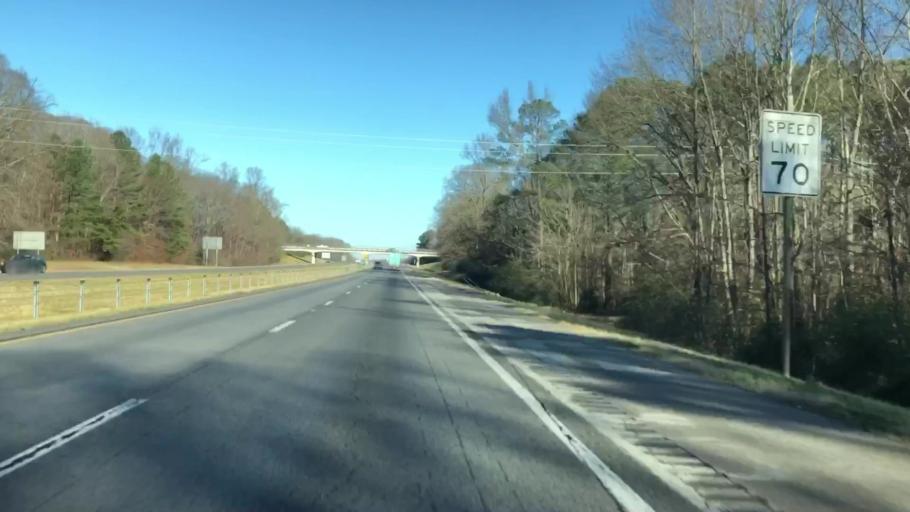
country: US
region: Alabama
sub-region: Limestone County
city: Athens
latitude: 34.7935
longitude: -86.9394
